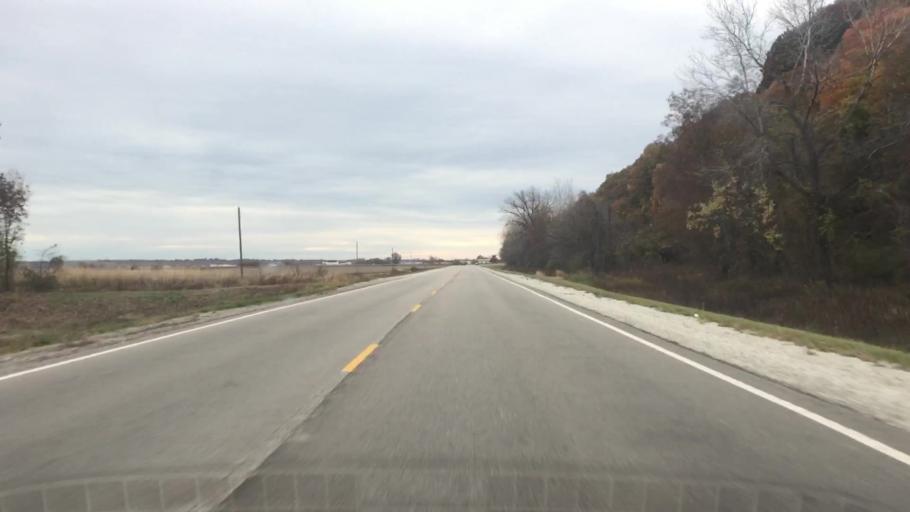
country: US
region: Missouri
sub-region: Cole County
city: Jefferson City
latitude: 38.5856
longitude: -92.1196
